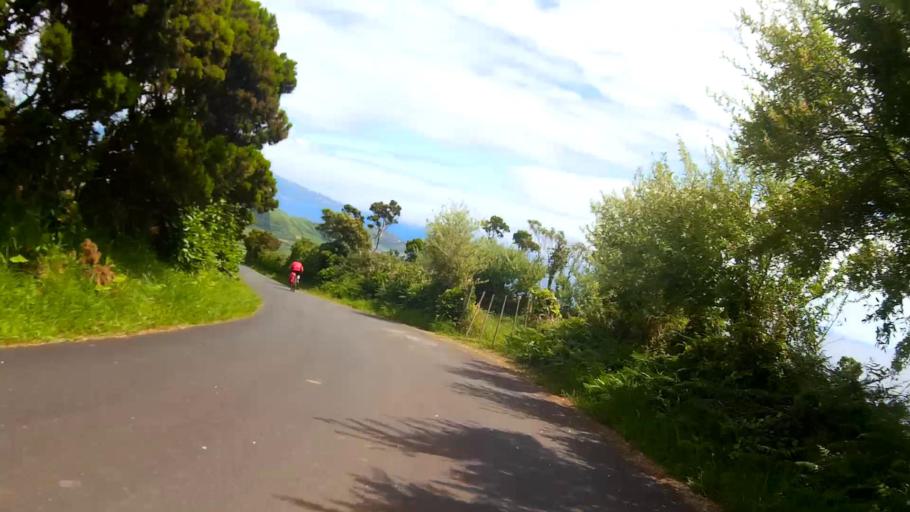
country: PT
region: Azores
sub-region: Horta
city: Horta
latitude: 38.5514
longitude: -28.6718
